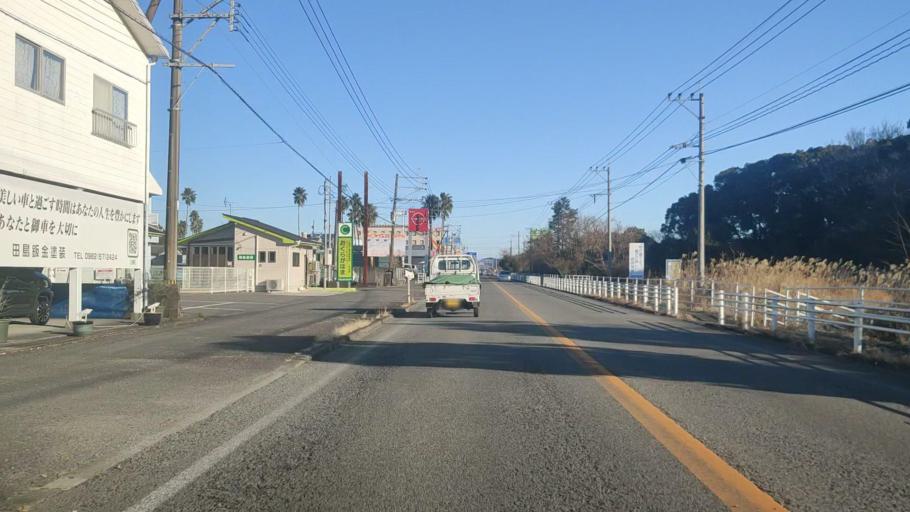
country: JP
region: Miyazaki
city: Nobeoka
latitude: 32.3917
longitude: 131.6279
